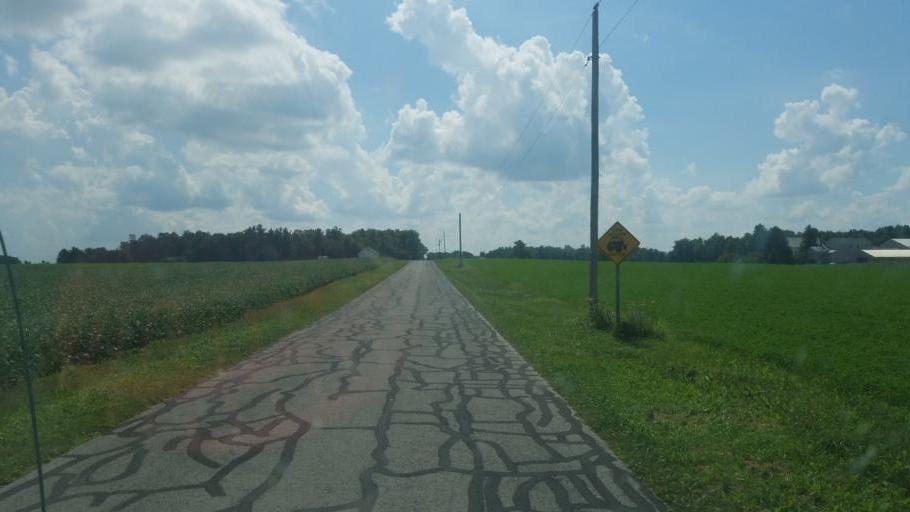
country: US
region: Ohio
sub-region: Hancock County
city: Arlington
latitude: 40.8920
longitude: -83.7080
